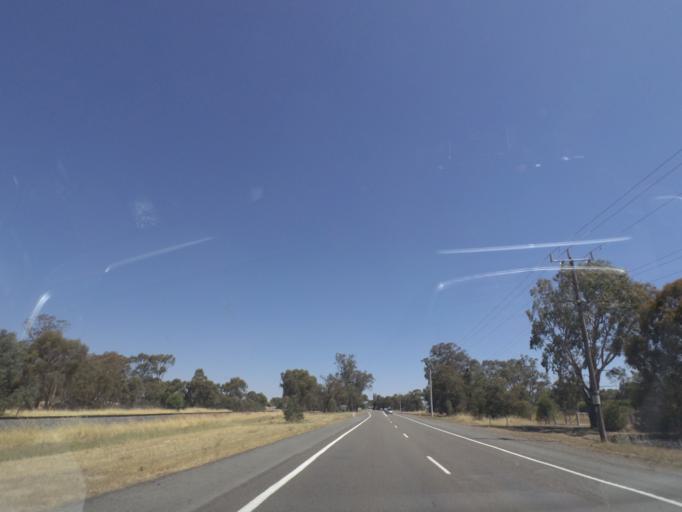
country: AU
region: Victoria
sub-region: Greater Shepparton
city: Shepparton
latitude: -36.2343
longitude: 145.4318
